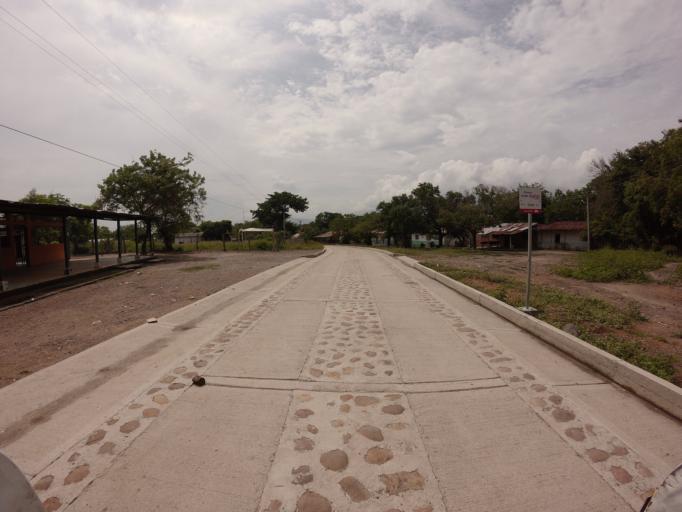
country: CO
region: Tolima
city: Natagaima
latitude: 3.4588
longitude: -75.1421
